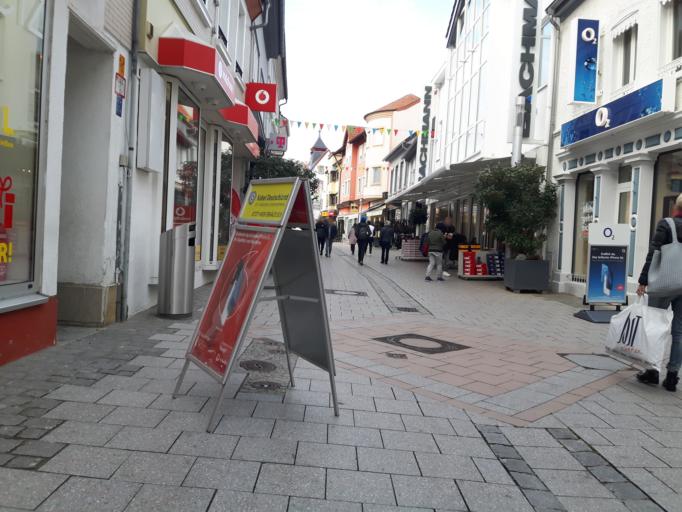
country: DE
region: Rheinland-Pfalz
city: Grunstadt
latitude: 49.5652
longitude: 8.1636
